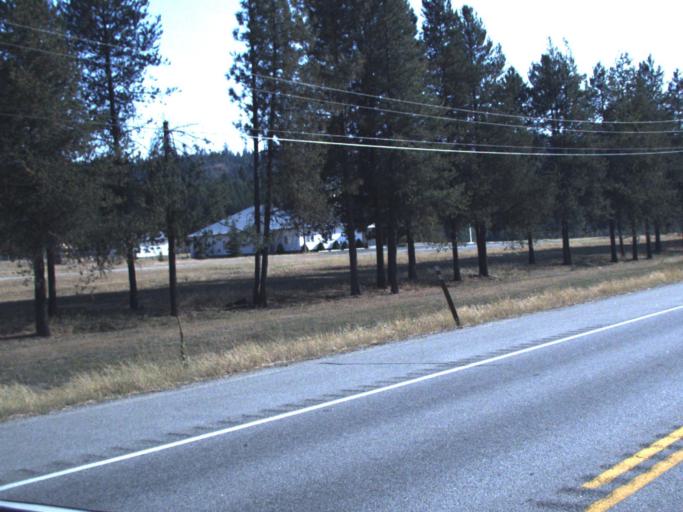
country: US
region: Washington
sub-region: Pend Oreille County
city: Newport
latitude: 48.1635
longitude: -117.0839
